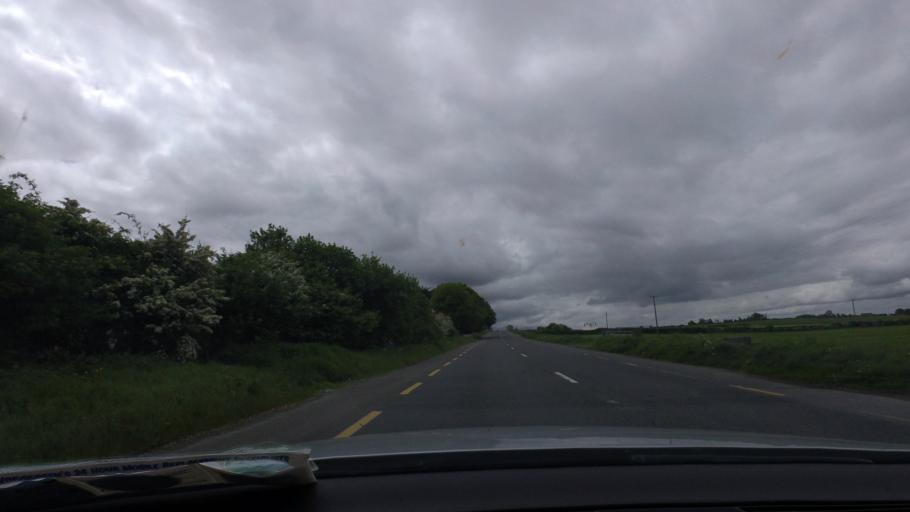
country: IE
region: Munster
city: Cashel
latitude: 52.5279
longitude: -7.8802
